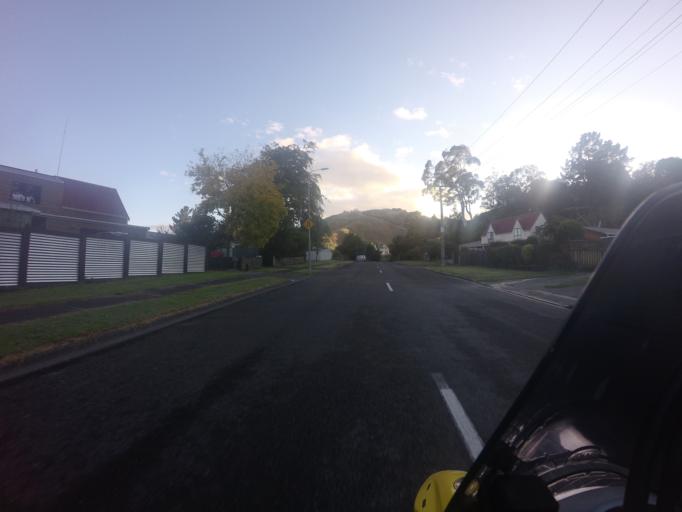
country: NZ
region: Gisborne
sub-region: Gisborne District
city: Gisborne
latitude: -38.6632
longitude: 178.0554
